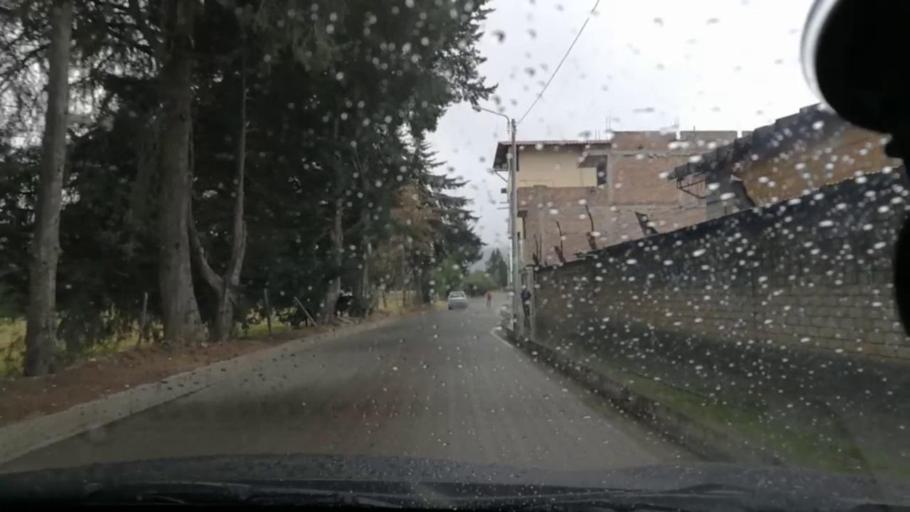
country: PE
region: Cajamarca
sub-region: Provincia de Cajamarca
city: Cajamarca
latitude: -7.1644
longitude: -78.4702
